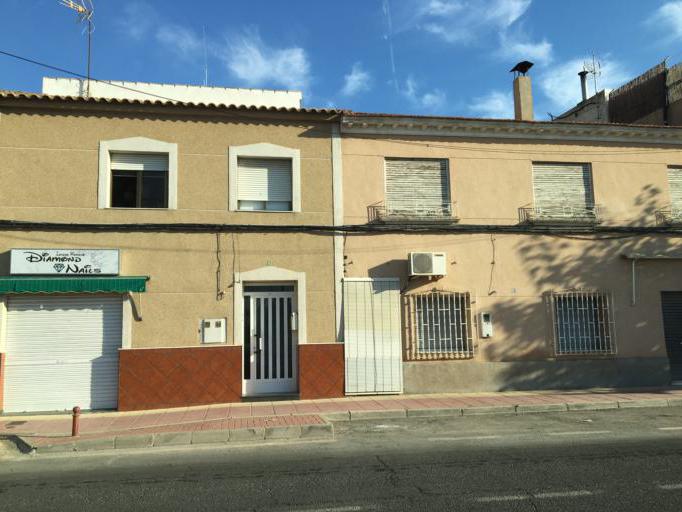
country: ES
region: Murcia
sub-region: Murcia
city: Murcia
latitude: 38.0172
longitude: -1.1475
